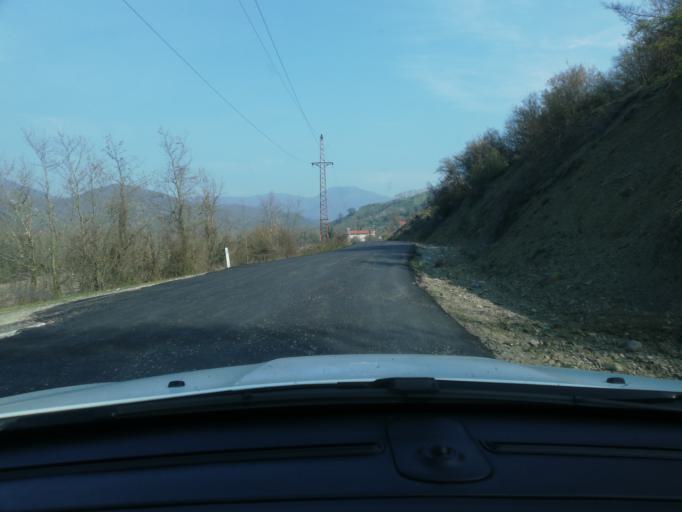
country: TR
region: Karabuk
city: Yenice
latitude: 41.2348
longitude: 32.3604
